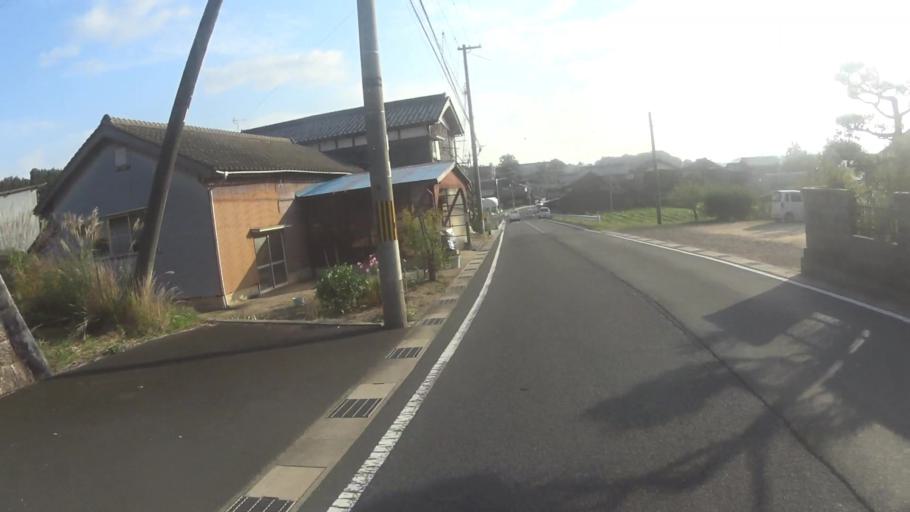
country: JP
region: Kyoto
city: Miyazu
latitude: 35.6755
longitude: 135.0962
